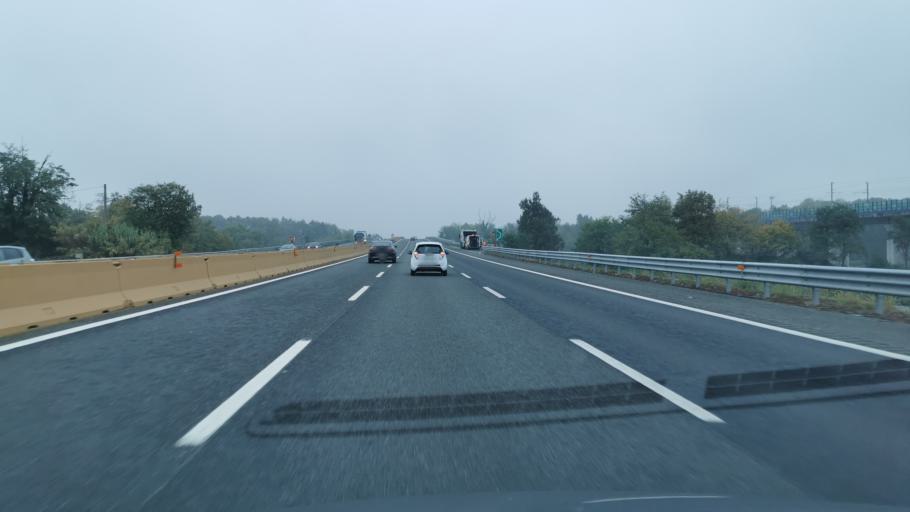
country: IT
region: Piedmont
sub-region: Provincia di Vercelli
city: Santhia
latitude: 45.3958
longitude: 8.1535
